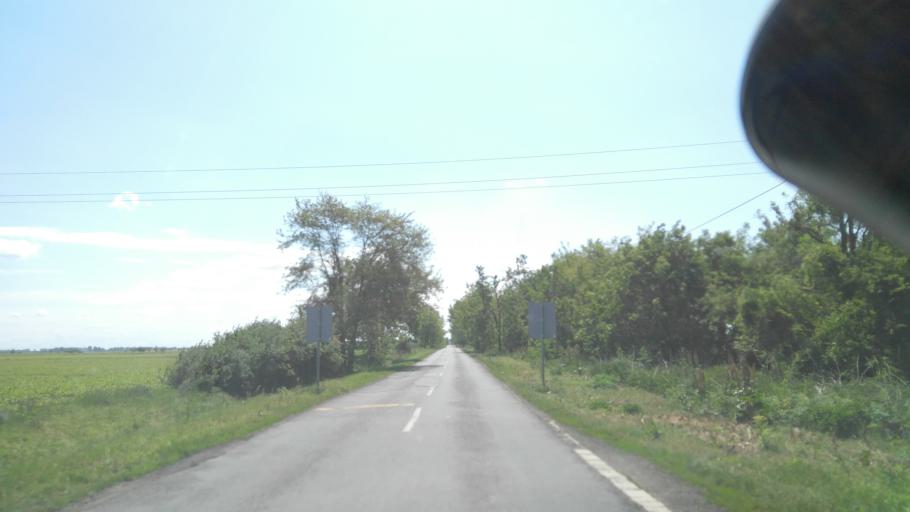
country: HU
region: Bekes
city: Magyarbanhegyes
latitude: 46.4427
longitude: 20.9872
